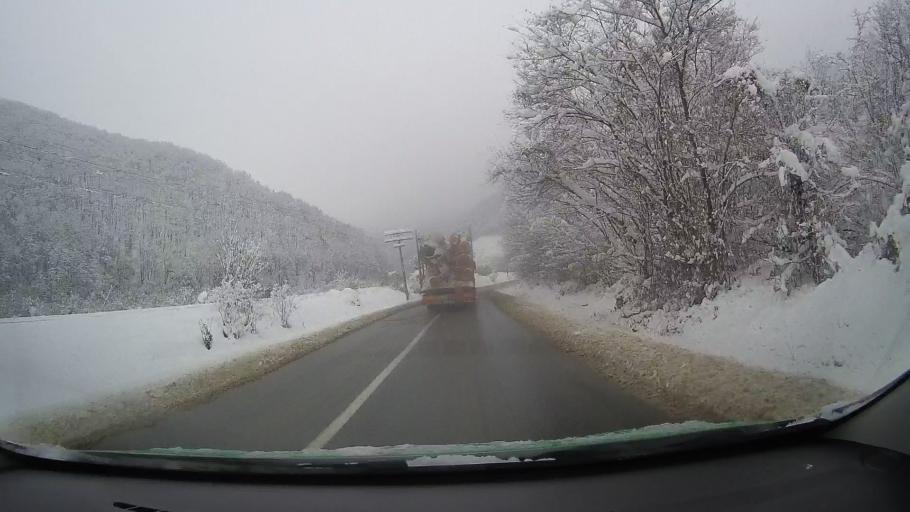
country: RO
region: Sibiu
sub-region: Comuna Orlat
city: Orlat
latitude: 45.7639
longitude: 23.9407
